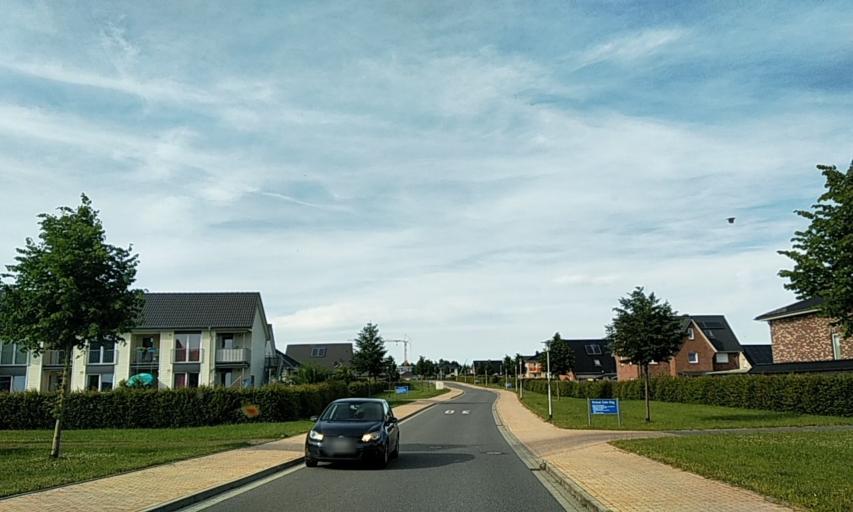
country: DE
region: Schleswig-Holstein
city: Schleswig
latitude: 54.5337
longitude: 9.5669
